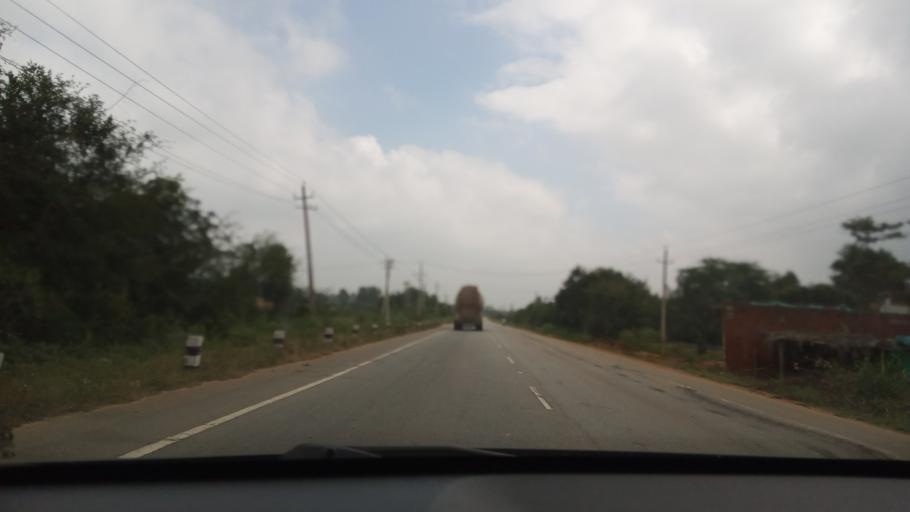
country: IN
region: Karnataka
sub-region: Chikkaballapur
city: Chintamani
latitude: 13.3655
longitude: 78.0509
